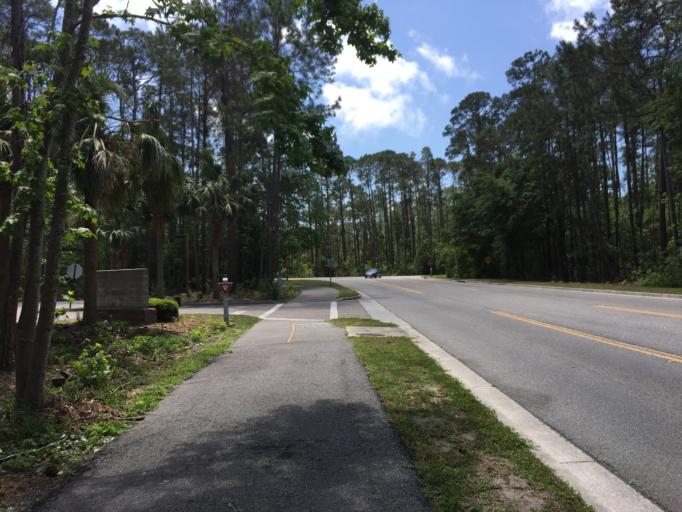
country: US
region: South Carolina
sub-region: Beaufort County
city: Hilton Head Island
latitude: 32.1702
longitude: -80.7728
